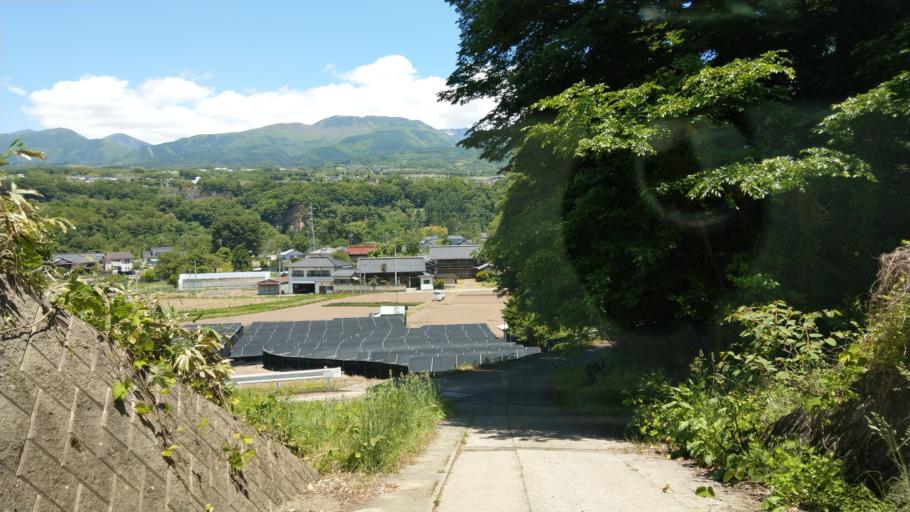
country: JP
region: Nagano
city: Komoro
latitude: 36.3286
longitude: 138.3991
